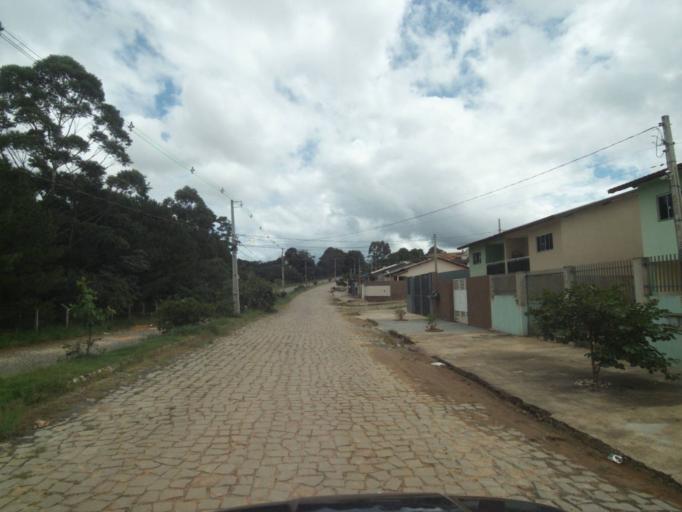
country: BR
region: Parana
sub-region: Telemaco Borba
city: Telemaco Borba
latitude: -24.3099
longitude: -50.6349
